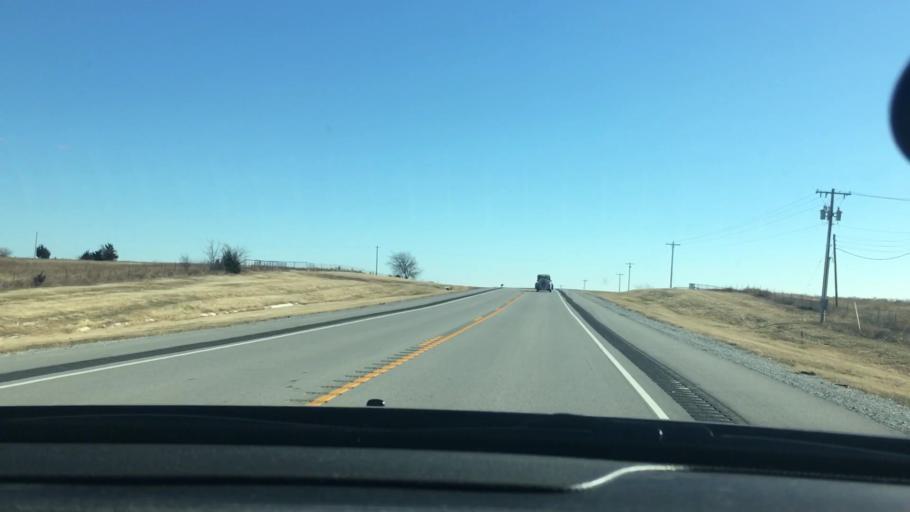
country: US
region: Oklahoma
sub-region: Love County
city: Marietta
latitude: 33.9403
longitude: -97.2330
